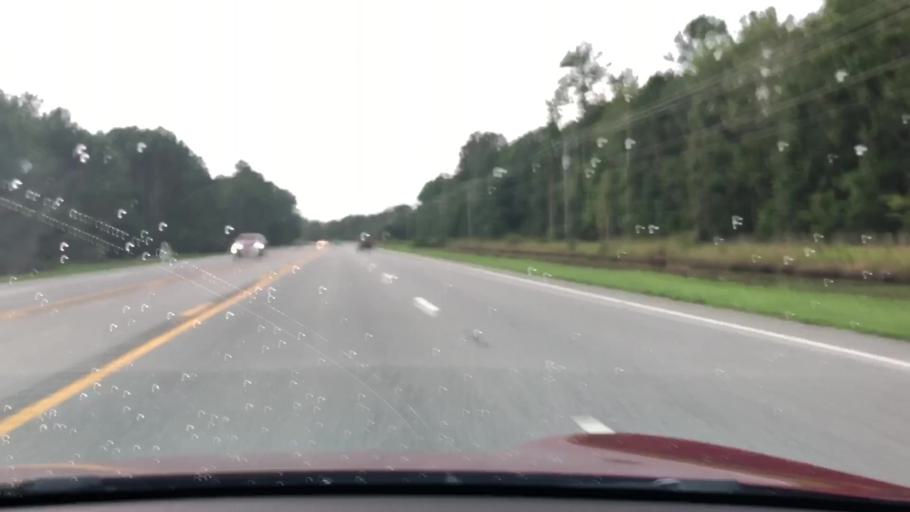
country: US
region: North Carolina
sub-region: Currituck County
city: Currituck
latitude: 36.4533
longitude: -76.0630
